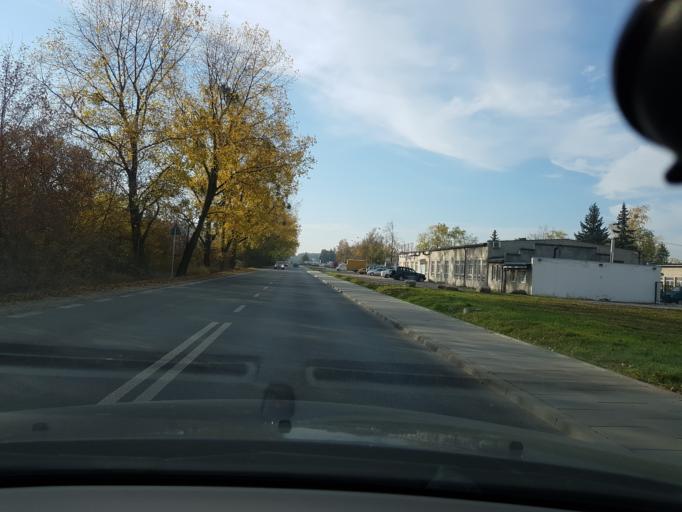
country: PL
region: Masovian Voivodeship
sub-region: Powiat warszawski zachodni
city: Babice
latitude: 52.2847
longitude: 20.8762
